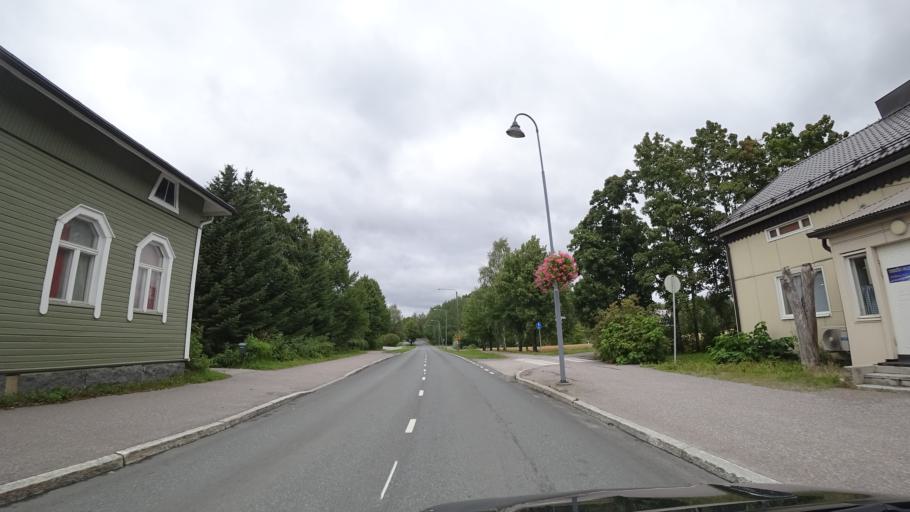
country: FI
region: Haeme
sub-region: Haemeenlinna
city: Lammi
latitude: 61.0811
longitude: 25.0124
